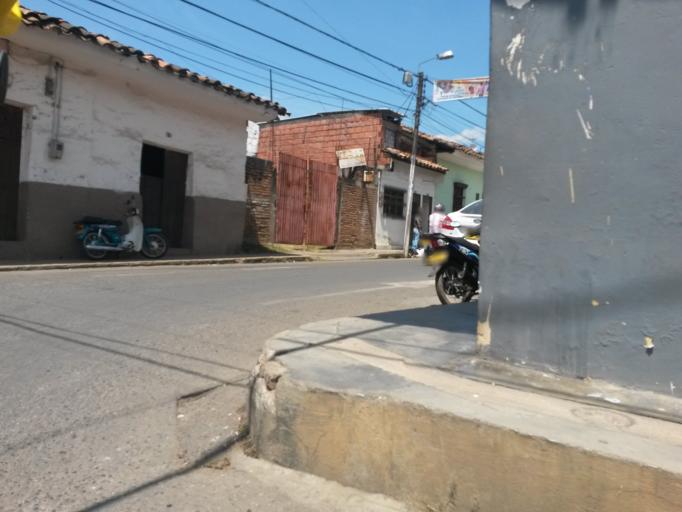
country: CO
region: Cauca
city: Santander de Quilichao
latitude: 3.0089
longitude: -76.4824
